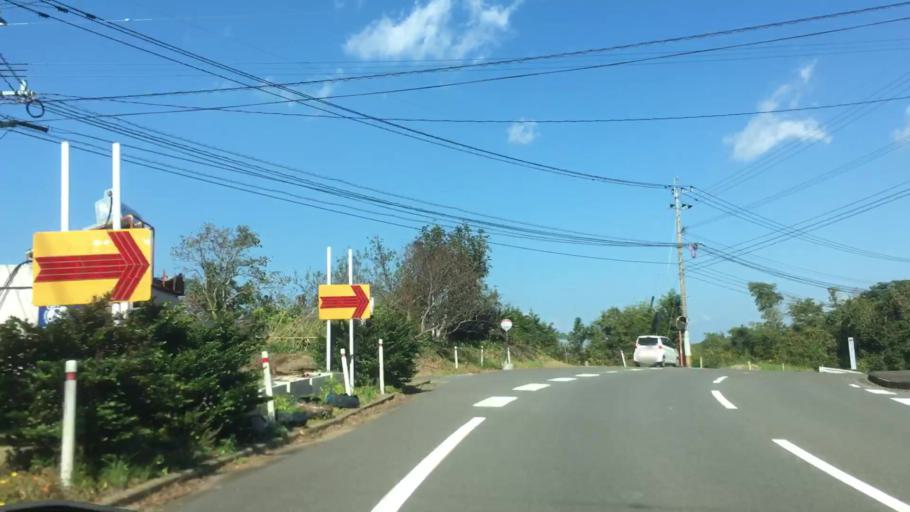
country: JP
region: Nagasaki
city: Sasebo
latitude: 33.0057
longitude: 129.6567
